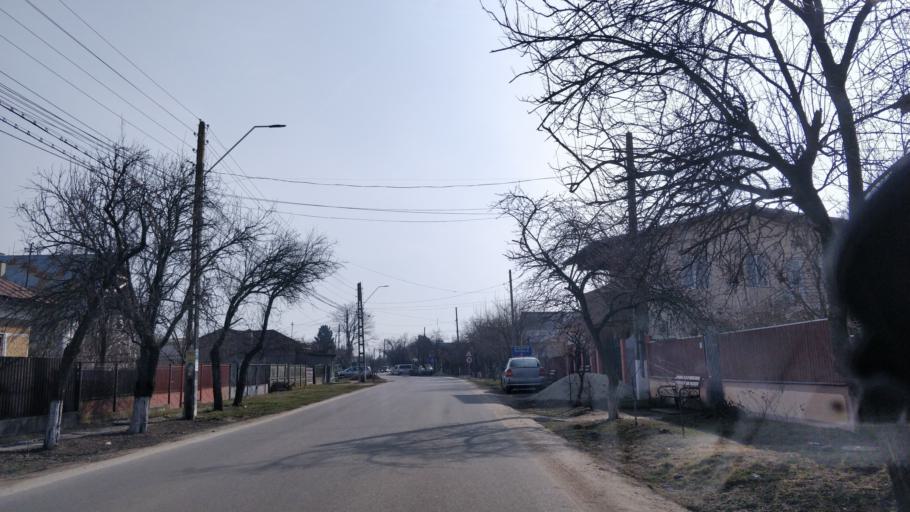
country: RO
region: Giurgiu
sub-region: Comuna Ulmi
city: Ulmi
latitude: 44.4871
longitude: 25.7820
